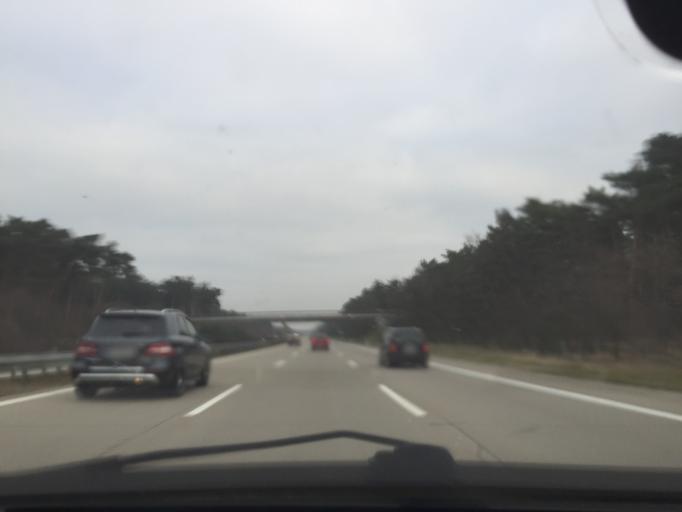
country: DE
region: Brandenburg
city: Wollin
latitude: 52.3145
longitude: 12.4873
